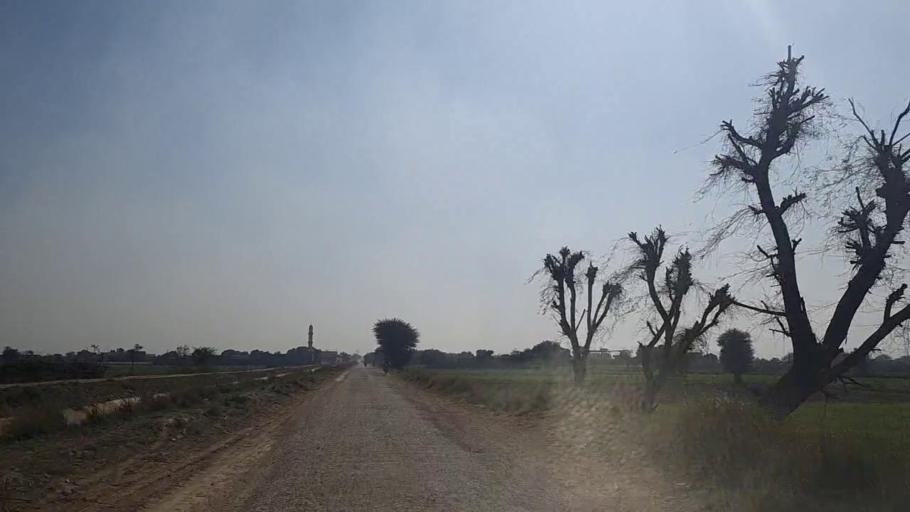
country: PK
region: Sindh
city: Shahpur Chakar
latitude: 26.1928
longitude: 68.5835
